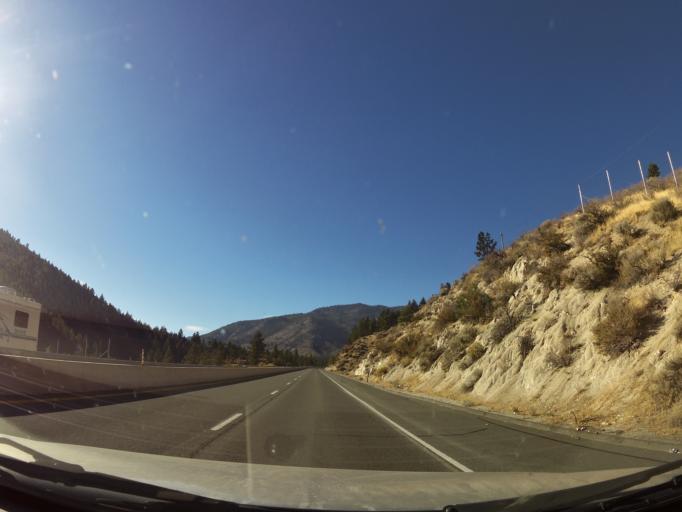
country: US
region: Nevada
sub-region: Douglas County
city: Indian Hills
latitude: 39.1145
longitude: -119.8076
